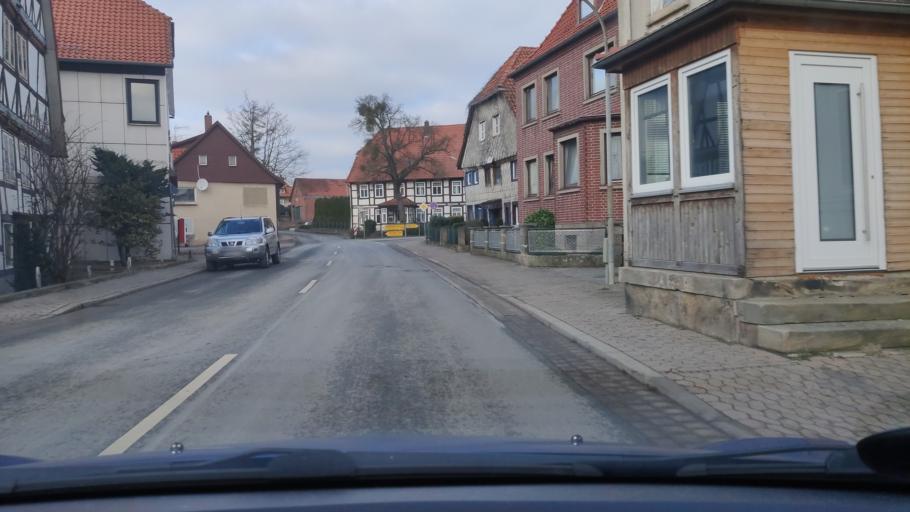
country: DE
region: Lower Saxony
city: Coppenbrugge
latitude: 52.1216
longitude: 9.5483
